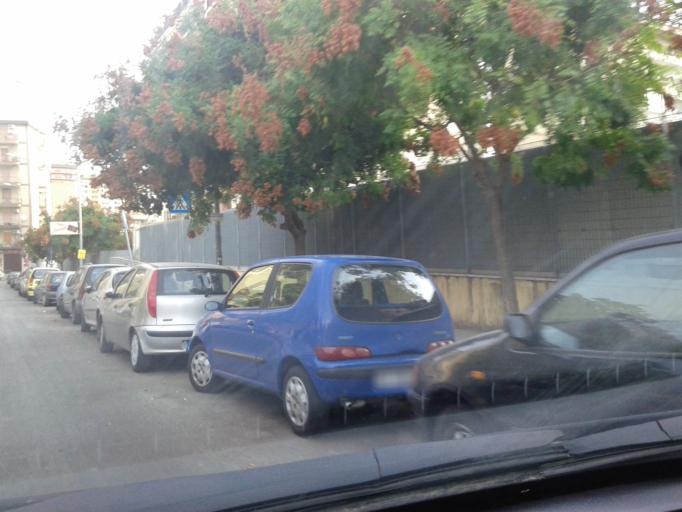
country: IT
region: Sicily
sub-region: Palermo
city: Palermo
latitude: 38.1099
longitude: 13.3424
